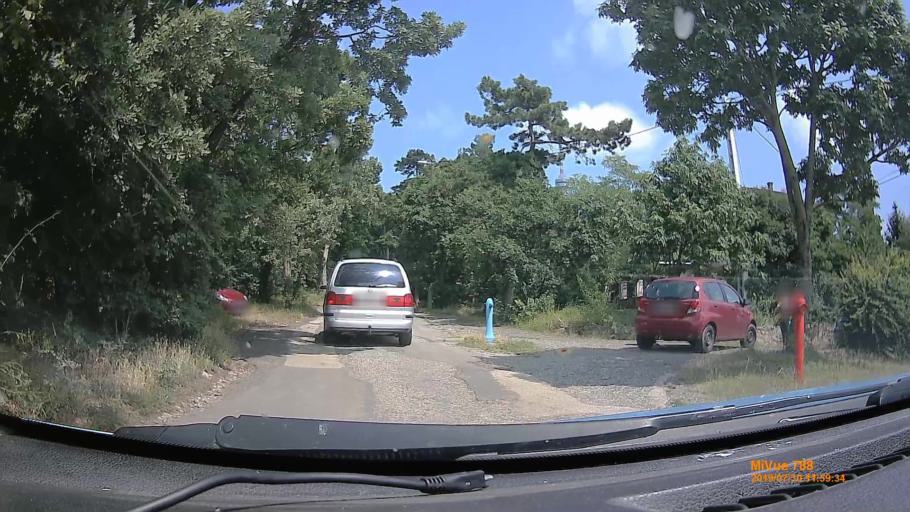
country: HU
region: Baranya
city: Pecs
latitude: 46.0899
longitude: 18.2158
